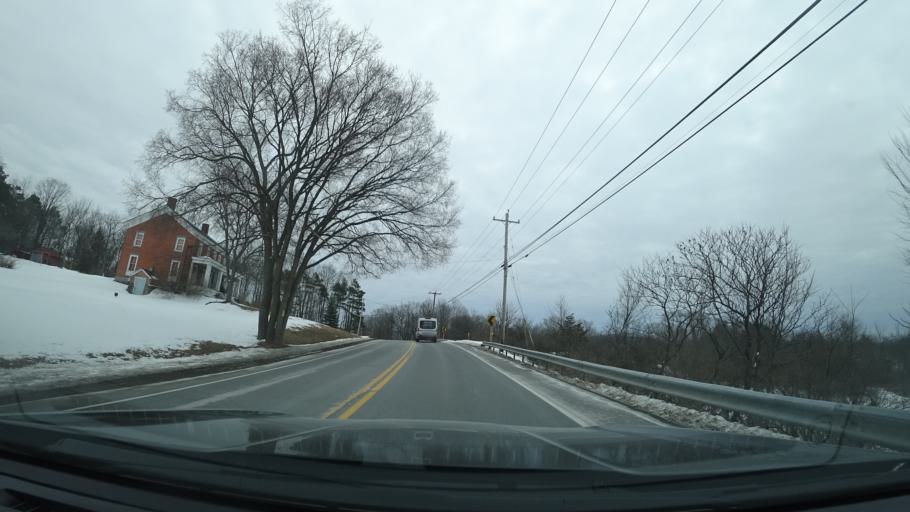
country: US
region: New York
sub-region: Washington County
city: Fort Edward
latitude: 43.2502
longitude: -73.4997
